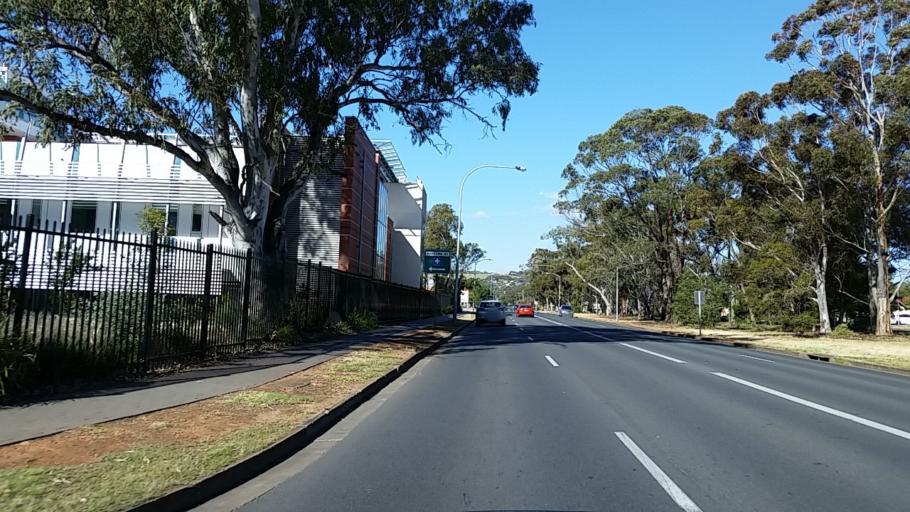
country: AU
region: South Australia
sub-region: Salisbury
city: Elizabeth
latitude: -34.7493
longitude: 138.6651
